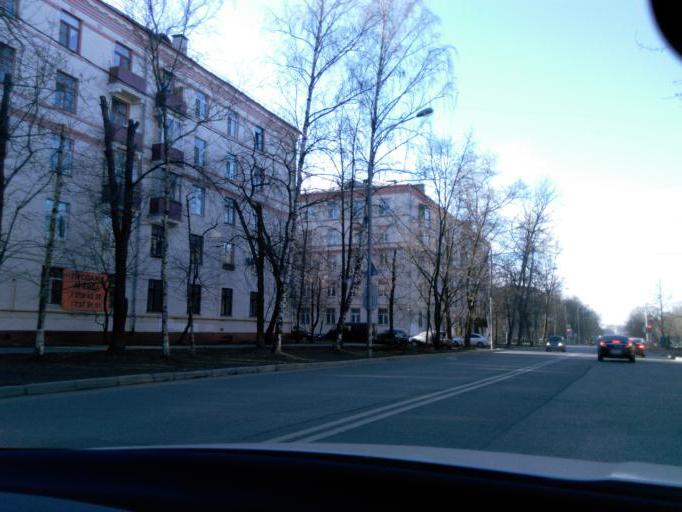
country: RU
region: Moskovskaya
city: Koptevo
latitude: 55.8382
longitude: 37.5225
